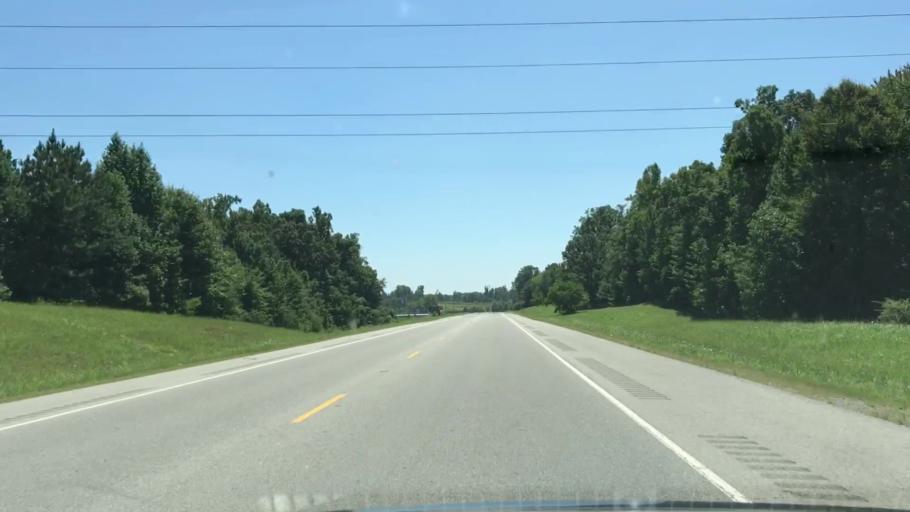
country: US
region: Tennessee
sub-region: Putnam County
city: Baxter
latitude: 36.1464
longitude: -85.6287
